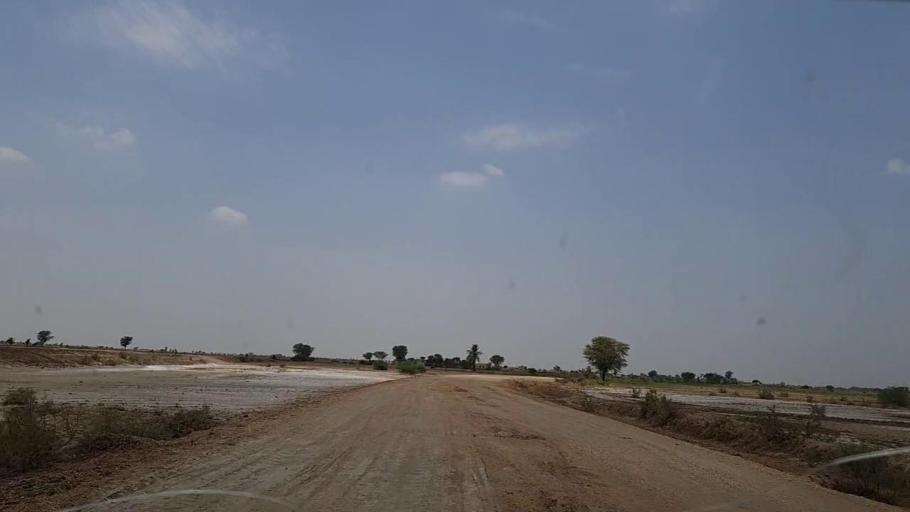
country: PK
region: Sindh
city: Phulji
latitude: 26.8028
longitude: 67.6344
